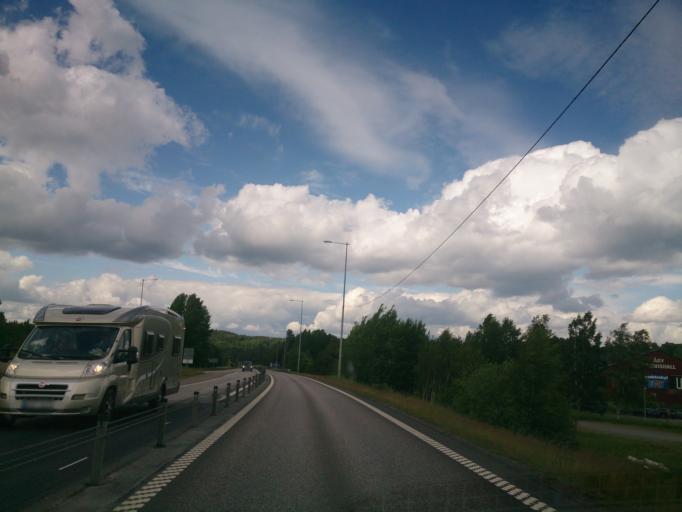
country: SE
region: OEstergoetland
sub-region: Norrkopings Kommun
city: Jursla
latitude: 58.6573
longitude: 16.1703
